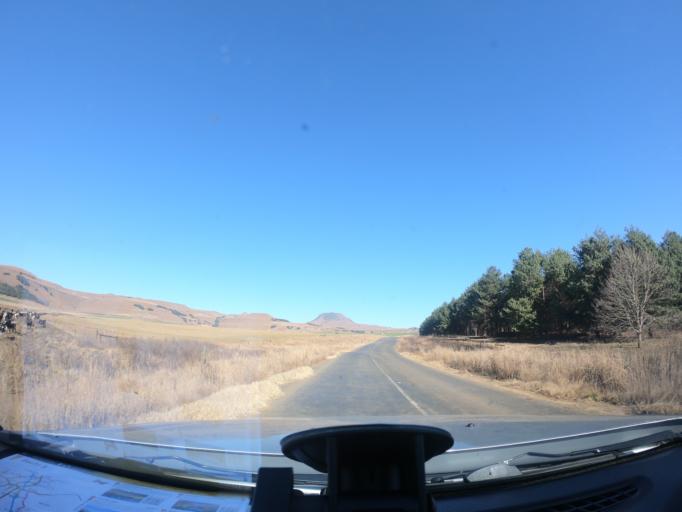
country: ZA
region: KwaZulu-Natal
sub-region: uMgungundlovu District Municipality
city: Mooirivier
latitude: -29.3324
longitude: 29.8185
